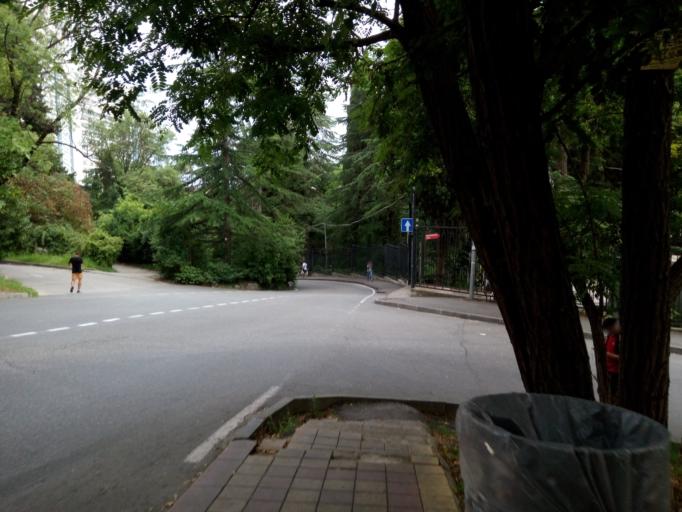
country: RU
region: Krasnodarskiy
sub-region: Sochi City
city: Sochi
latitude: 43.5648
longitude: 39.7602
